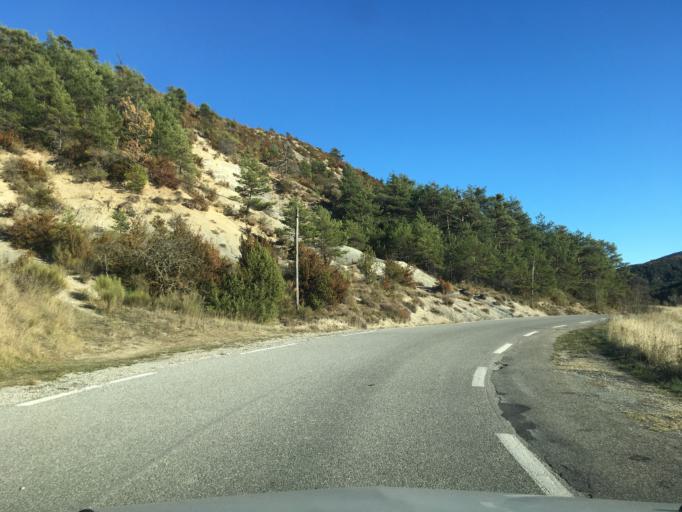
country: FR
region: Provence-Alpes-Cote d'Azur
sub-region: Departement des Alpes-de-Haute-Provence
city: Castellane
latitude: 43.7557
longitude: 6.4384
